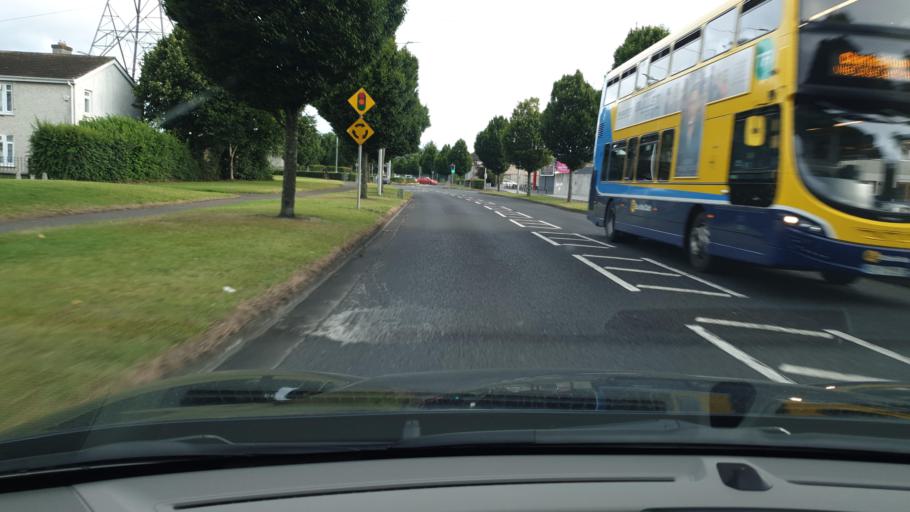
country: IE
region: Leinster
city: Clondalkin
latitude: 53.3393
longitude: -6.3999
